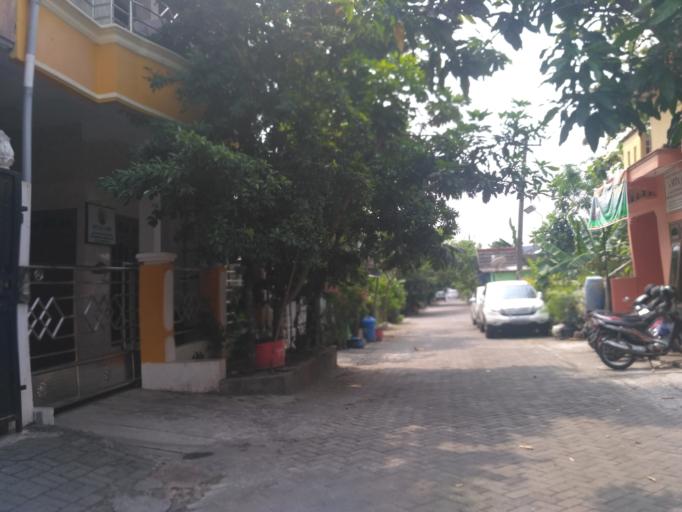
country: ID
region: Central Java
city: Mranggen
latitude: -7.0667
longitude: 110.4636
